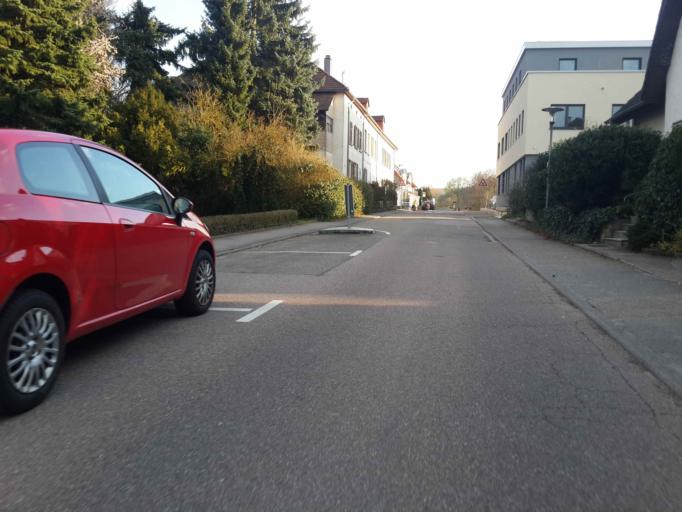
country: DE
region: Baden-Wuerttemberg
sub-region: Karlsruhe Region
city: Sinsheim
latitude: 49.2368
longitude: 8.9085
